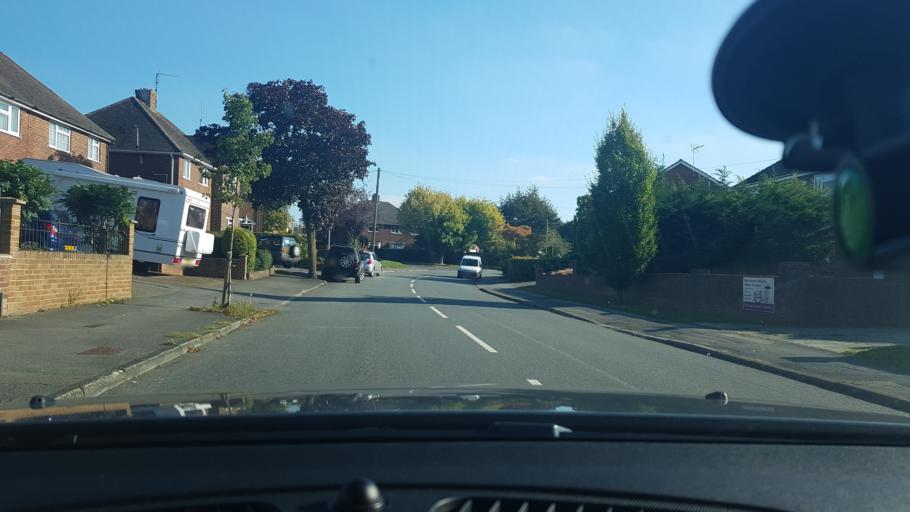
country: GB
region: England
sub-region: Gloucestershire
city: Gloucester
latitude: 51.8351
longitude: -2.2563
